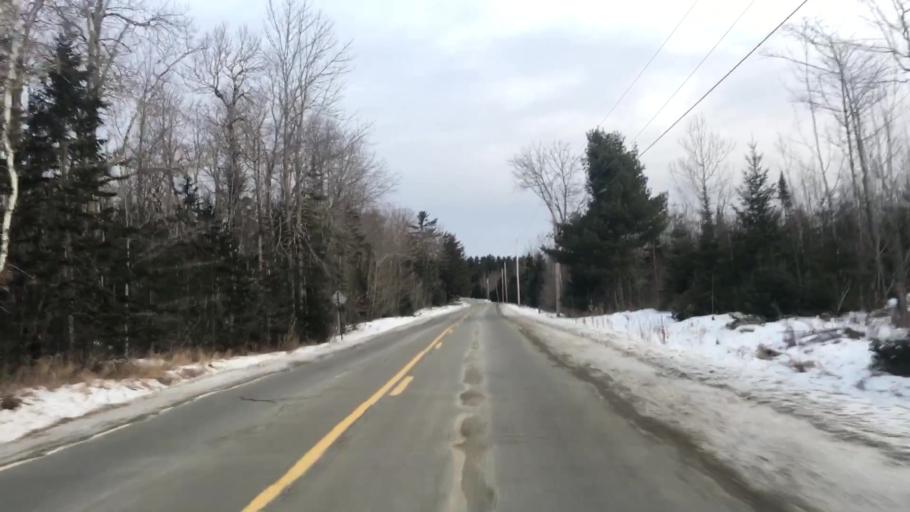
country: US
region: Maine
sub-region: Hancock County
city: Franklin
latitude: 44.7595
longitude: -68.3250
